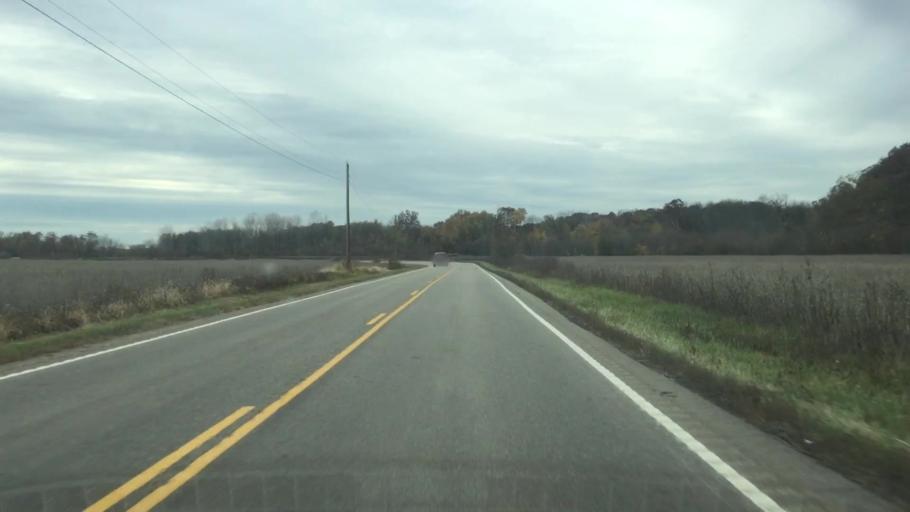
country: US
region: Missouri
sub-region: Callaway County
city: Fulton
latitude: 38.7083
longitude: -91.7514
